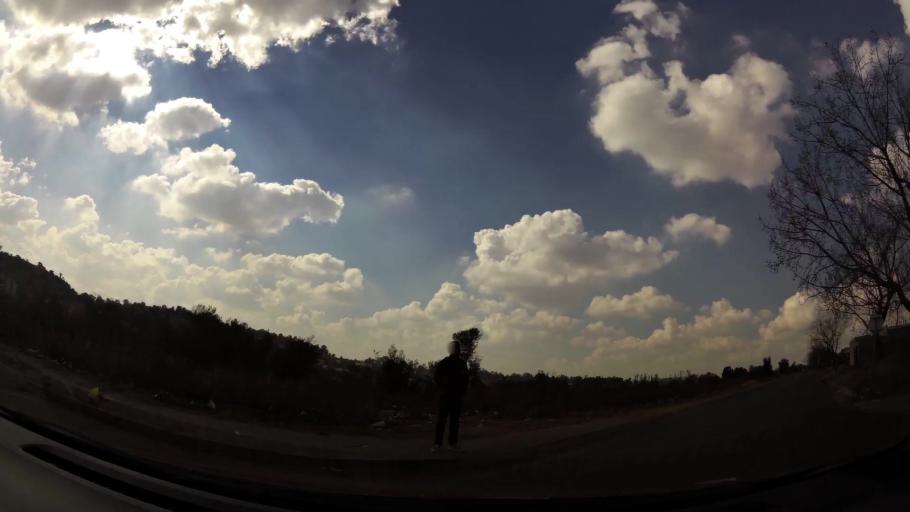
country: ZA
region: Gauteng
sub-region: City of Johannesburg Metropolitan Municipality
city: Roodepoort
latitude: -26.1815
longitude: 27.8540
